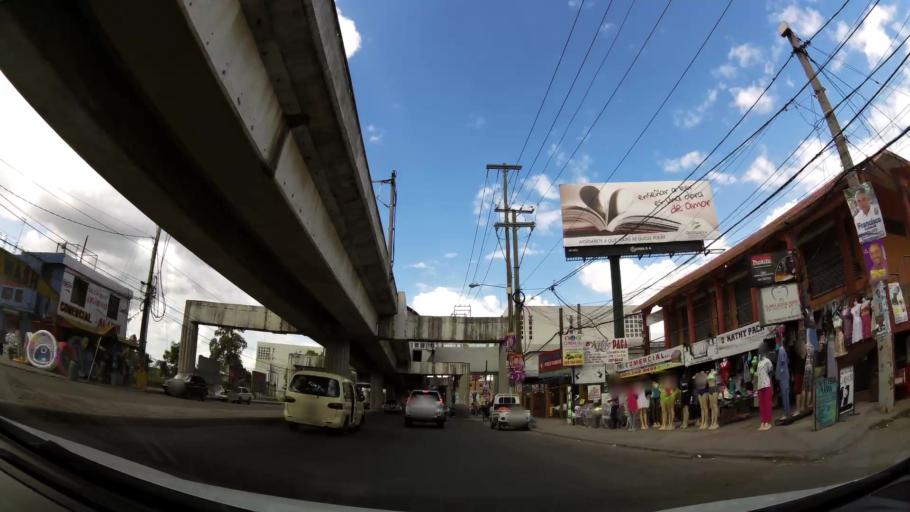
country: DO
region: Nacional
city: Ensanche Luperon
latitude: 18.5392
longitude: -69.9046
